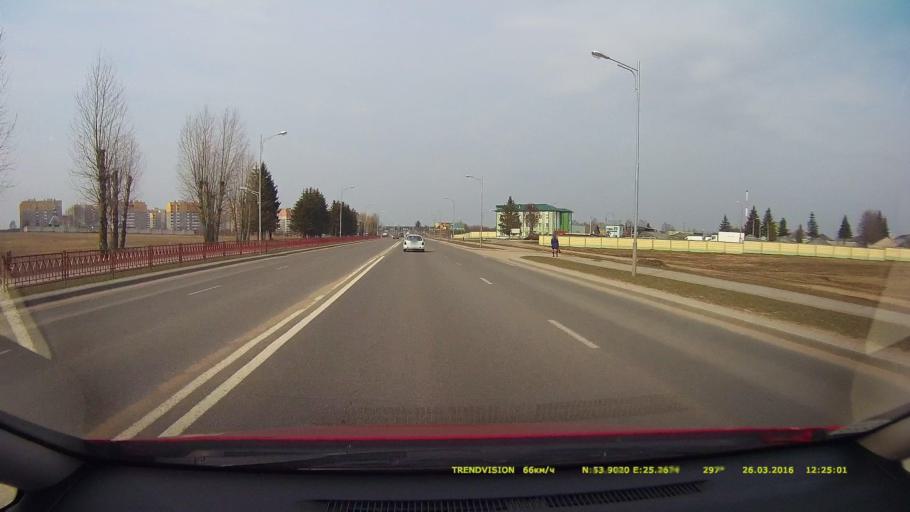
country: BY
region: Grodnenskaya
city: Lida
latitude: 53.9021
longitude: 25.2672
